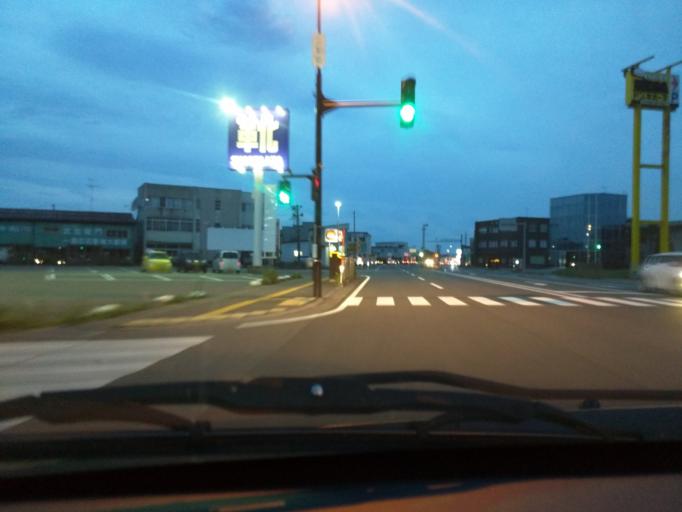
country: JP
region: Niigata
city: Kashiwazaki
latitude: 37.3649
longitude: 138.5784
